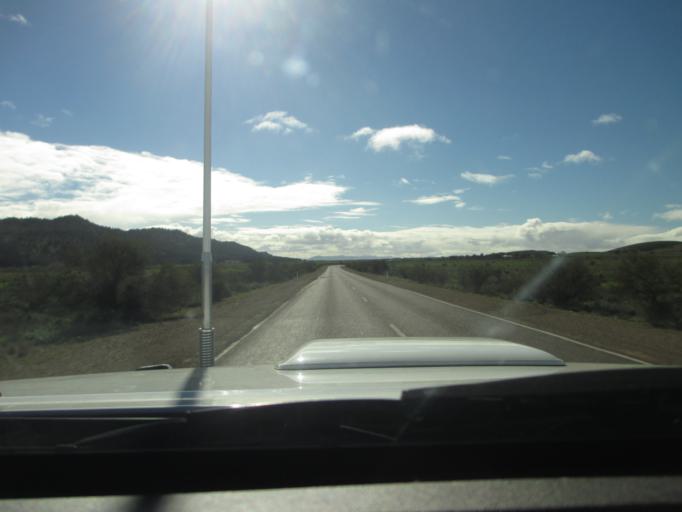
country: AU
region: South Australia
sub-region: Flinders Ranges
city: Quorn
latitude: -31.9422
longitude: 138.4031
